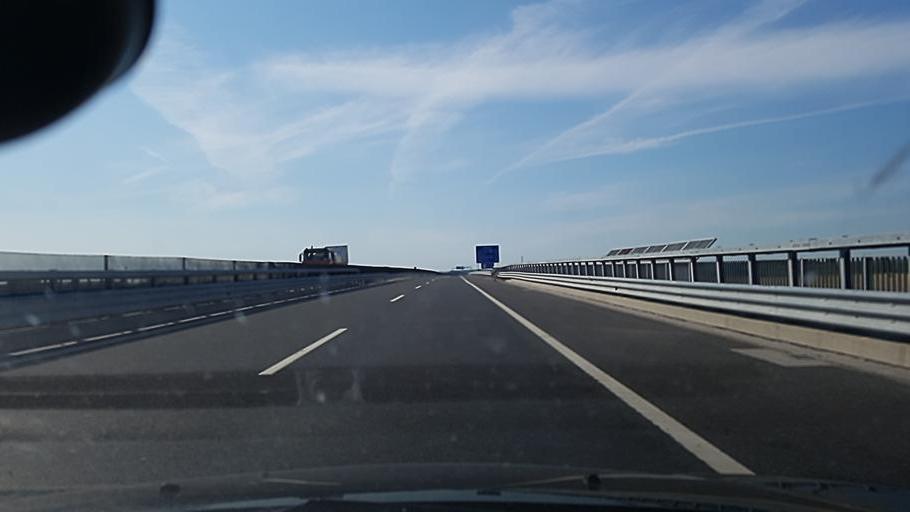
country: HU
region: Tolna
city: Tolna
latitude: 46.4047
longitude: 18.7432
